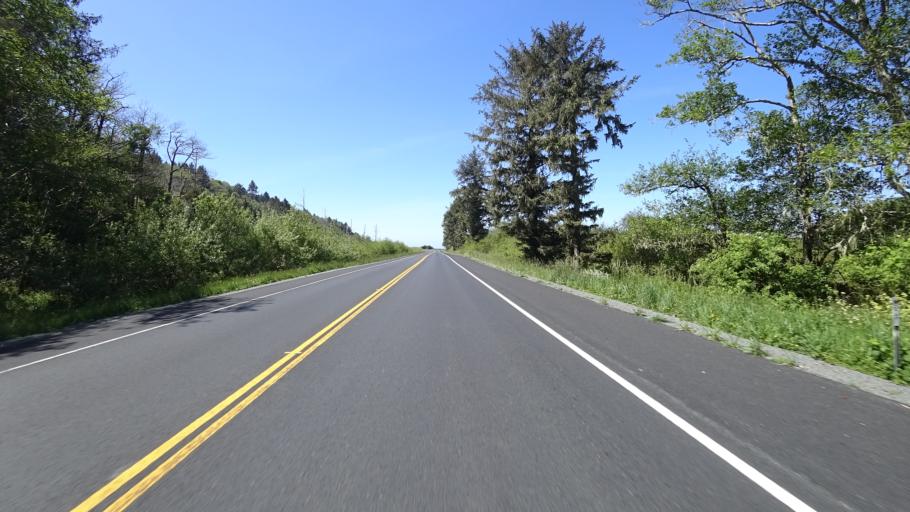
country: US
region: California
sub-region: Humboldt County
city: Westhaven-Moonstone
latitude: 41.2860
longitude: -124.0868
